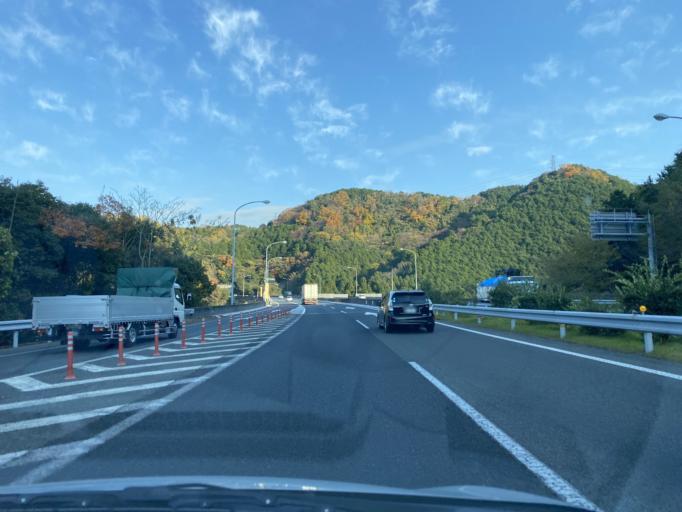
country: JP
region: Osaka
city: Izumi
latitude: 34.4040
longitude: 135.4367
